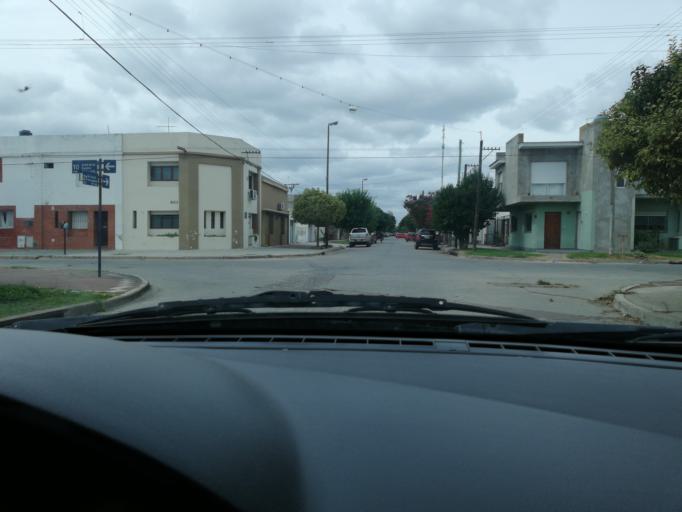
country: AR
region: Buenos Aires
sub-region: Partido de Balcarce
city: Balcarce
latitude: -37.8456
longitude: -58.2626
